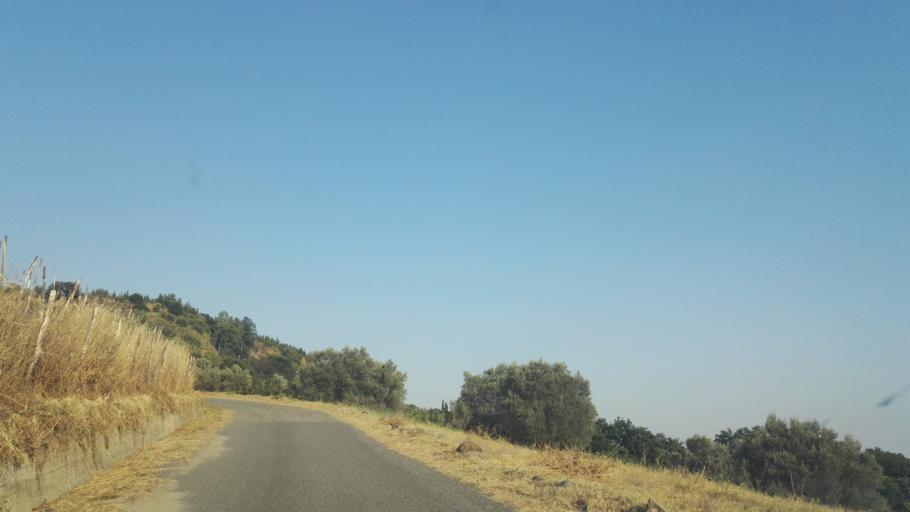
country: IT
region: Calabria
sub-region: Provincia di Reggio Calabria
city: Placanica
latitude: 38.4253
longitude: 16.4488
